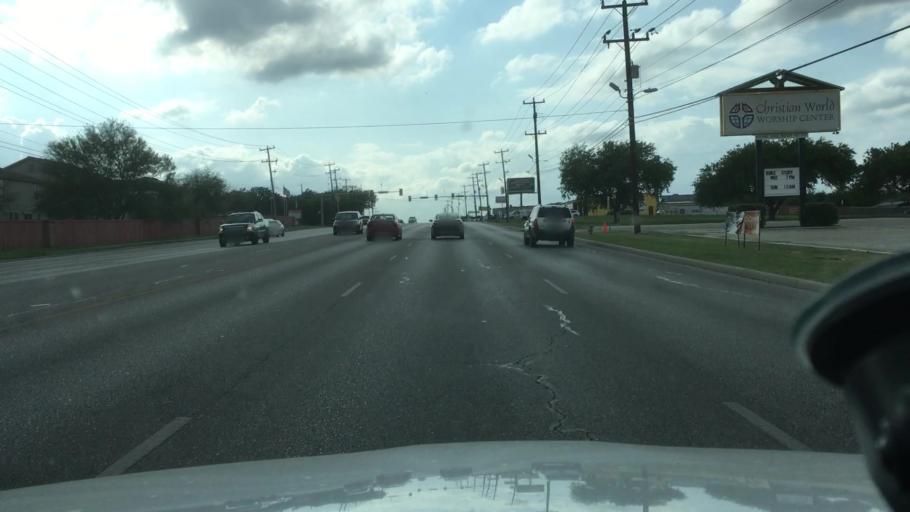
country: US
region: Texas
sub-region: Bexar County
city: Windcrest
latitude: 29.5013
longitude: -98.3576
